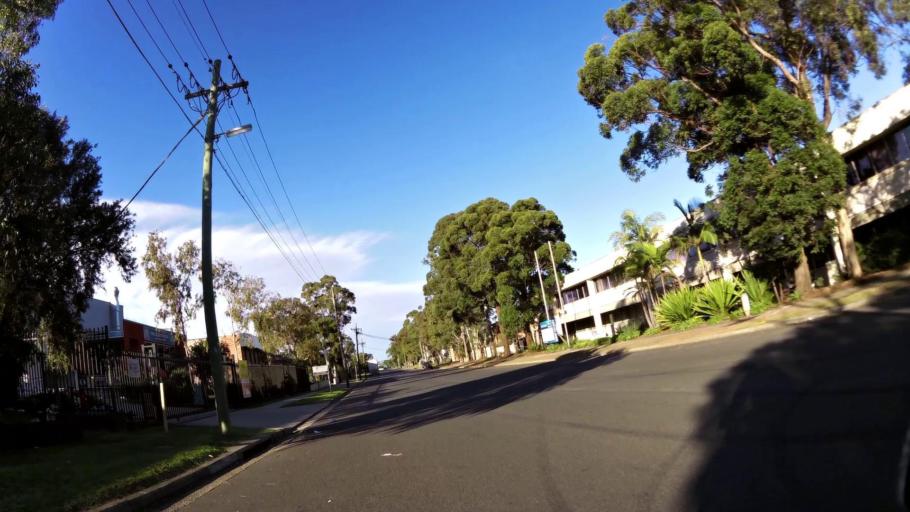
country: AU
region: New South Wales
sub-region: Bankstown
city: Milperra
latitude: -33.9200
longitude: 150.9987
